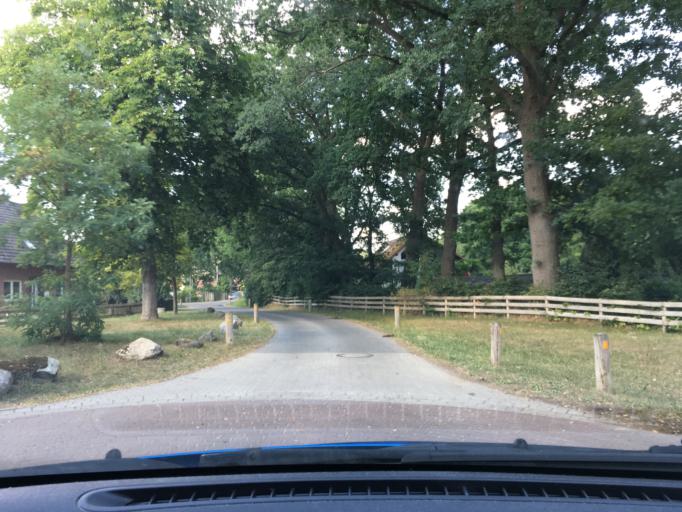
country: DE
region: Lower Saxony
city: Salzhausen
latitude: 53.2170
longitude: 10.1931
